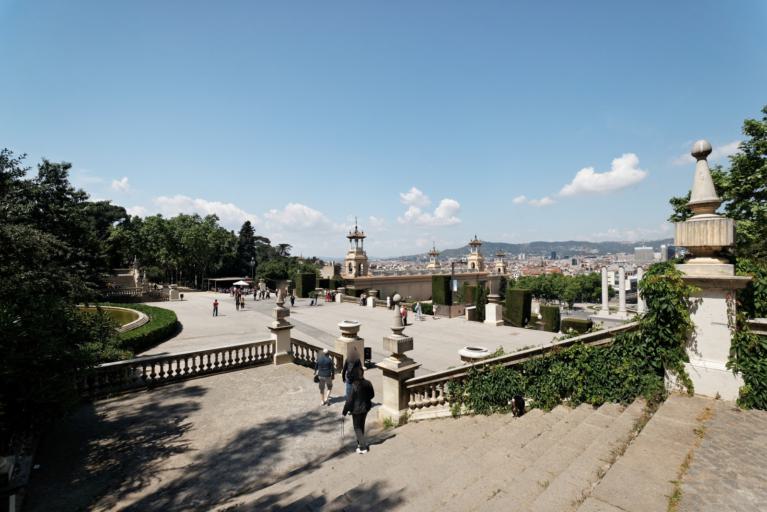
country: ES
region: Catalonia
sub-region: Provincia de Barcelona
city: Sants-Montjuic
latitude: 41.3695
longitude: 2.1533
